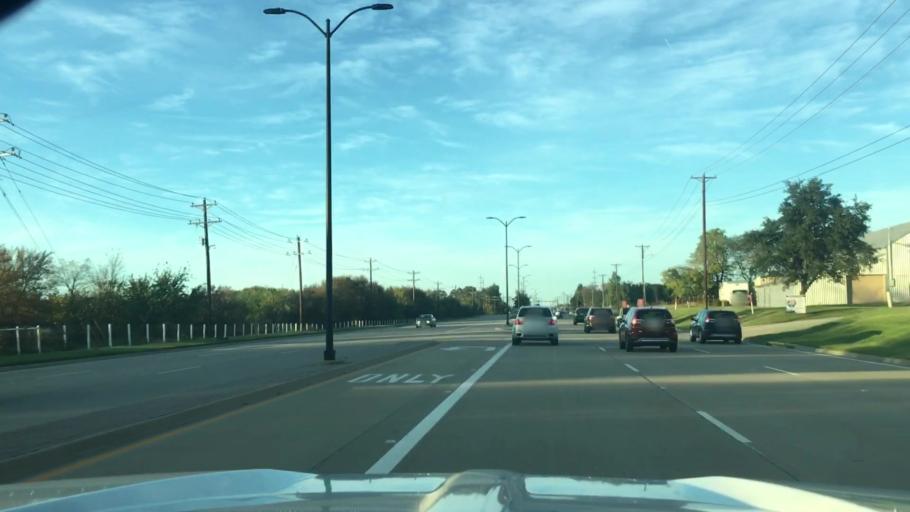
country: US
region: Texas
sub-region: Collin County
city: Frisco
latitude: 33.1823
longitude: -96.8030
